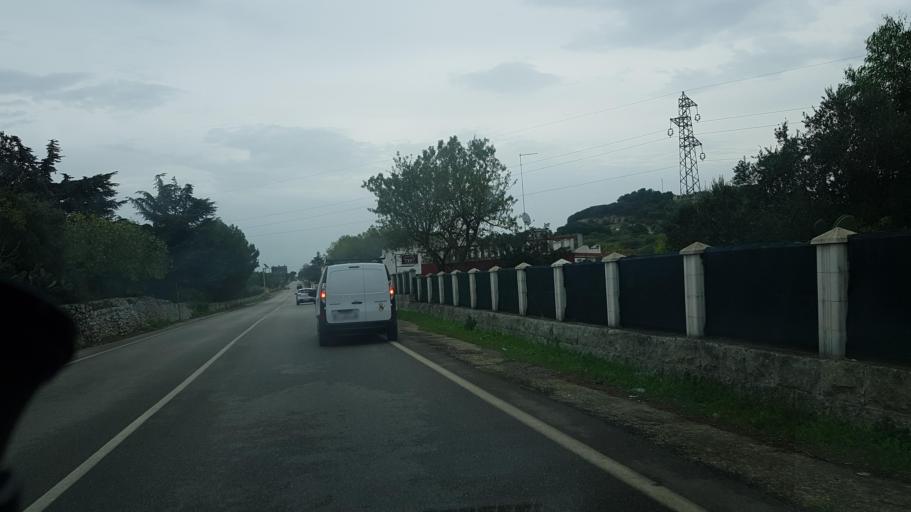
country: IT
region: Apulia
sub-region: Provincia di Brindisi
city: Ostuni
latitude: 40.7199
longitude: 17.6086
